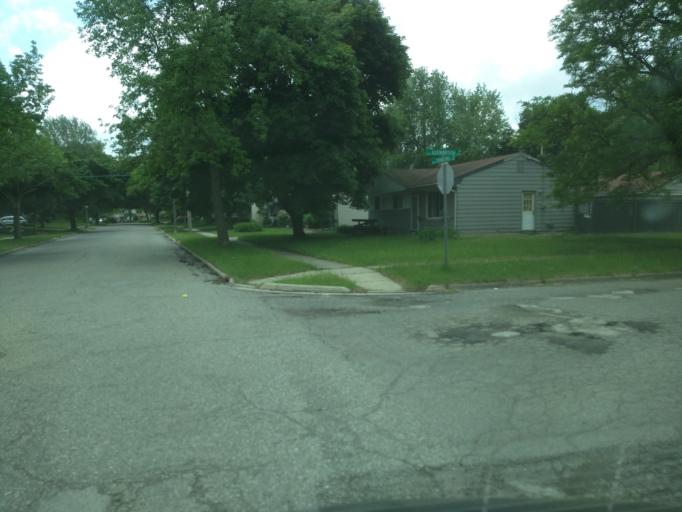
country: US
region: Michigan
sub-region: Eaton County
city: Waverly
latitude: 42.6963
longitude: -84.5944
